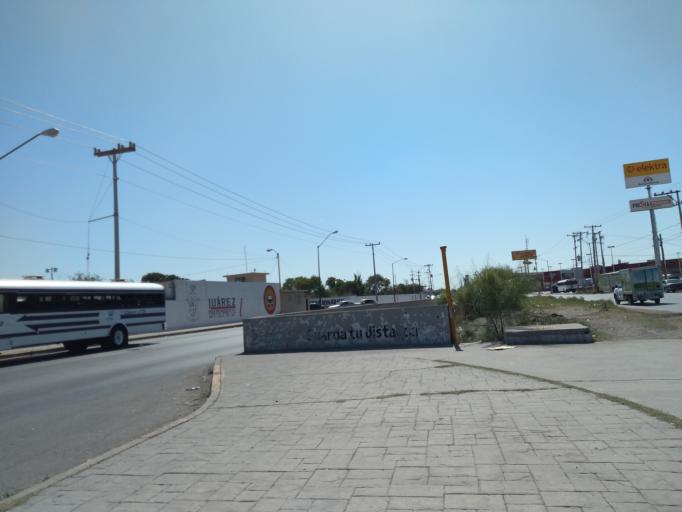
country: US
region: Texas
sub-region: El Paso County
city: El Paso
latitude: 31.7546
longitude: -106.5001
